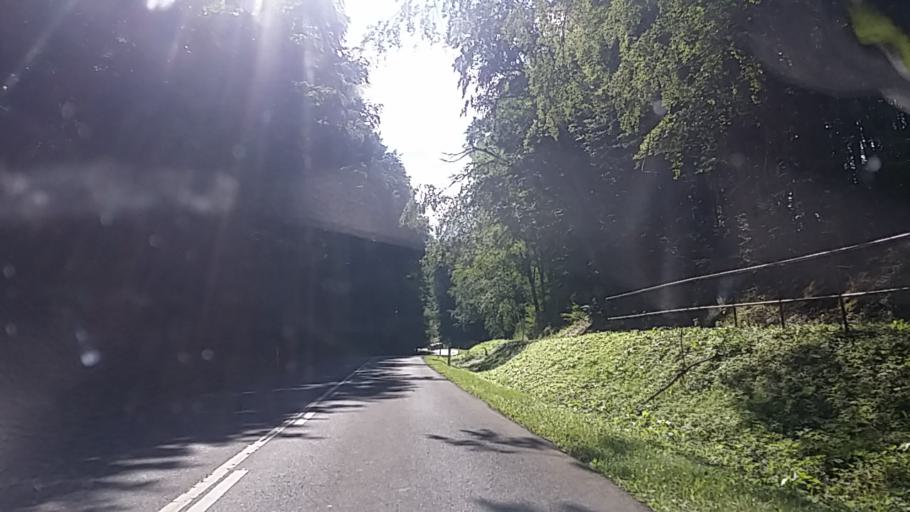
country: HU
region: Baranya
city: Pecs
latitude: 46.1275
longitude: 18.1626
